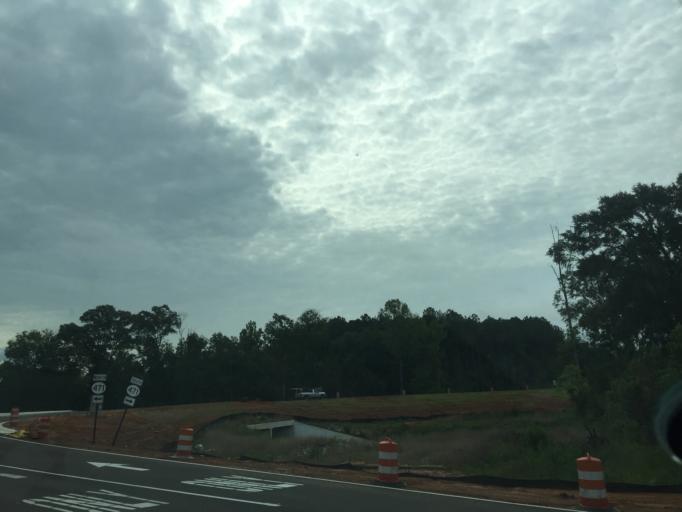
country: US
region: Mississippi
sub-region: Rankin County
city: Brandon
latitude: 32.2929
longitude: -89.9976
